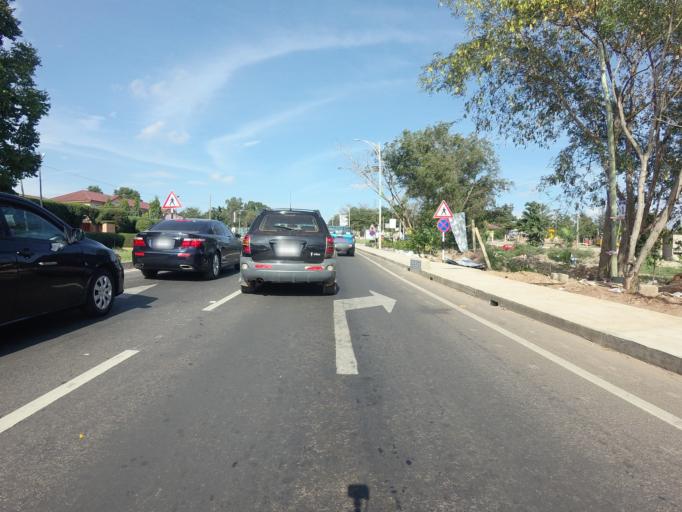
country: GH
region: Greater Accra
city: Medina Estates
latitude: 5.6304
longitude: -0.1578
